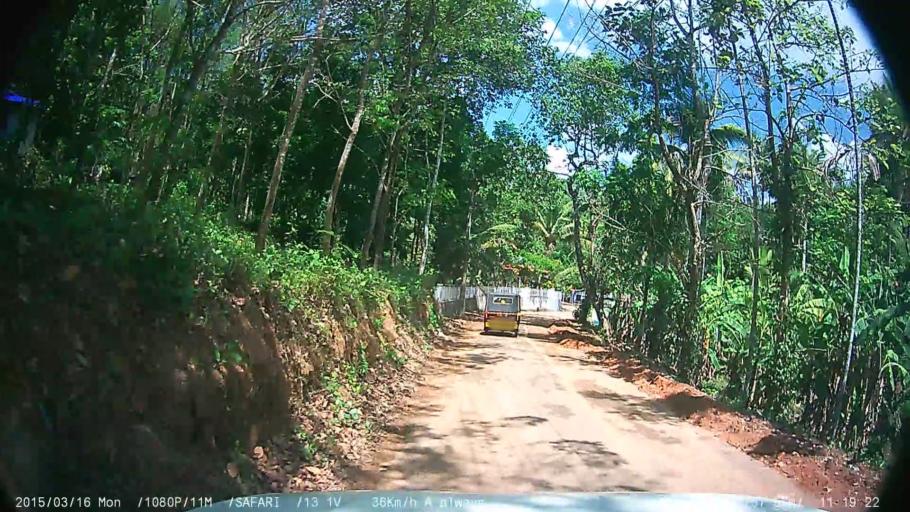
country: IN
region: Kerala
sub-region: Kottayam
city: Palackattumala
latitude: 9.7813
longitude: 76.5539
